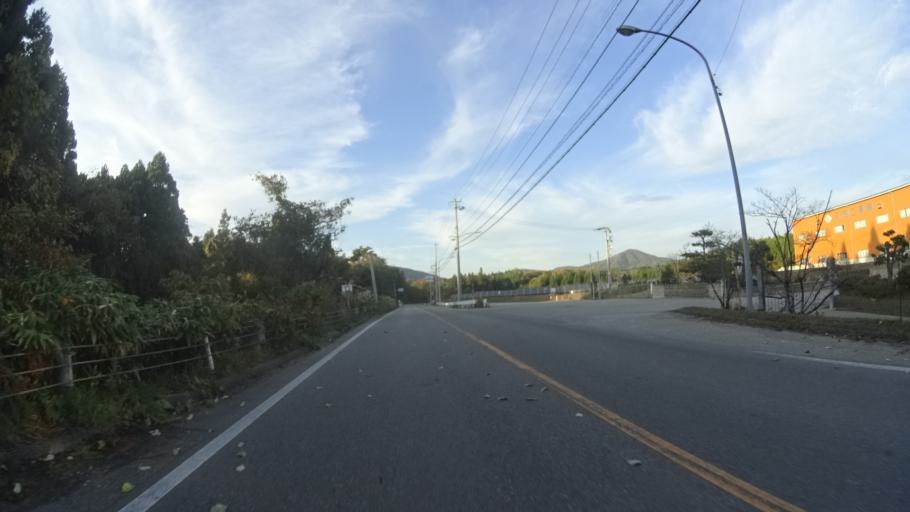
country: JP
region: Ishikawa
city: Nanao
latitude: 37.1732
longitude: 136.7137
